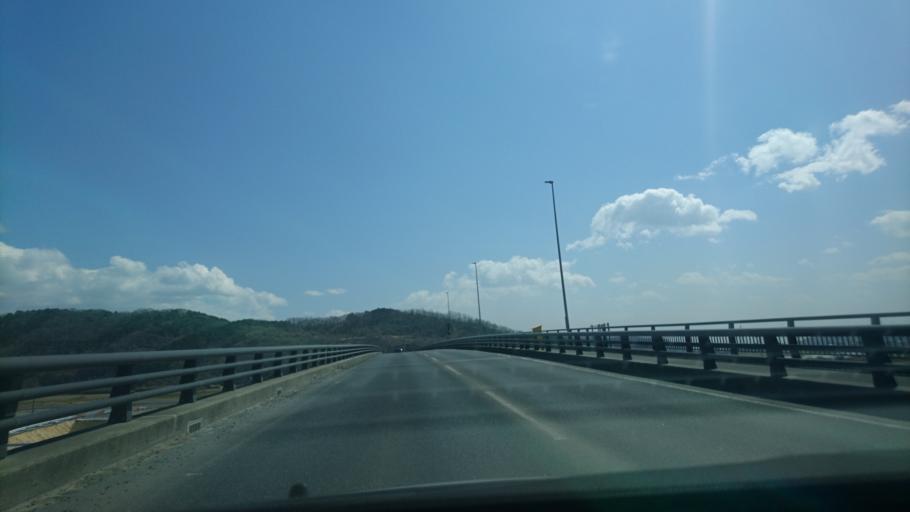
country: JP
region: Miyagi
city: Ishinomaki
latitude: 38.4589
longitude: 141.2860
